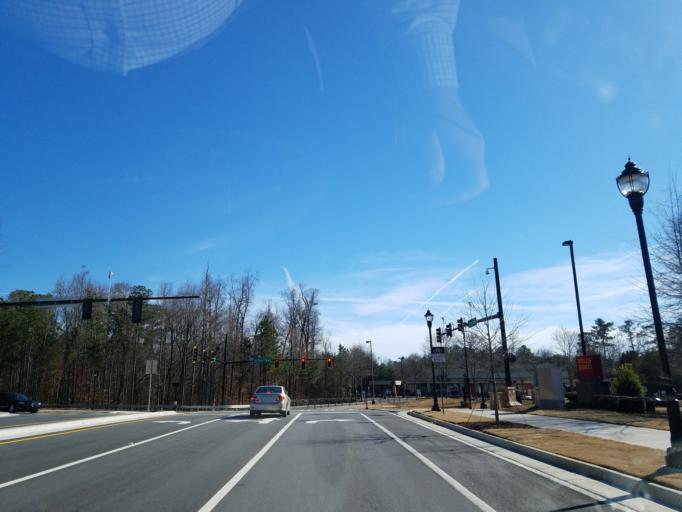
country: US
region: Georgia
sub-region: Fulton County
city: Alpharetta
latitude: 34.0444
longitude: -84.3000
